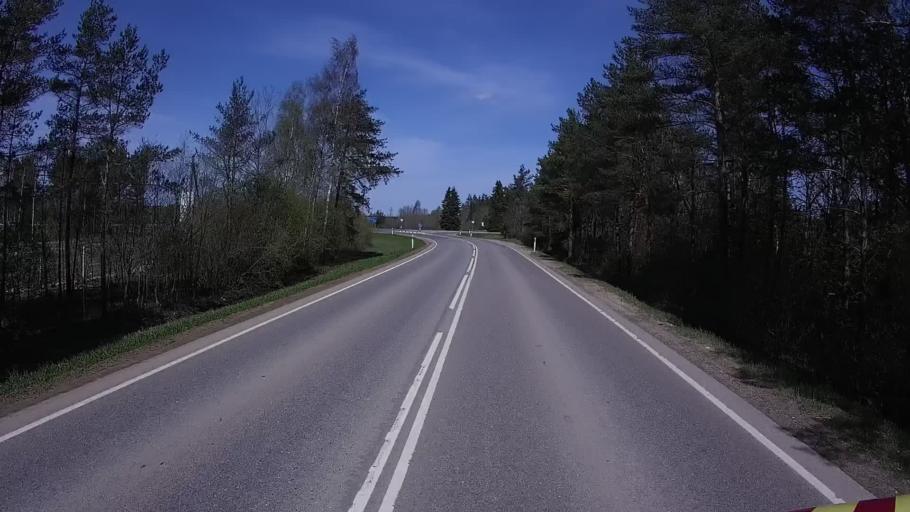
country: EE
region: Harju
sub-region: Keila linn
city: Keila
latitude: 59.3270
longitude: 24.3279
